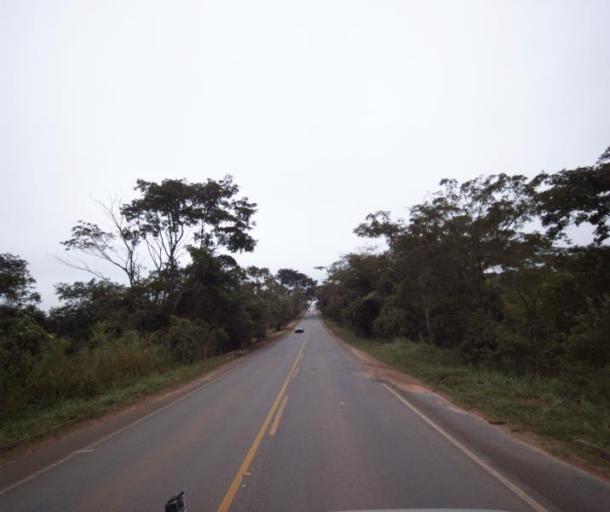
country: BR
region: Goias
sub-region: Pirenopolis
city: Pirenopolis
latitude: -15.9781
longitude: -48.8266
